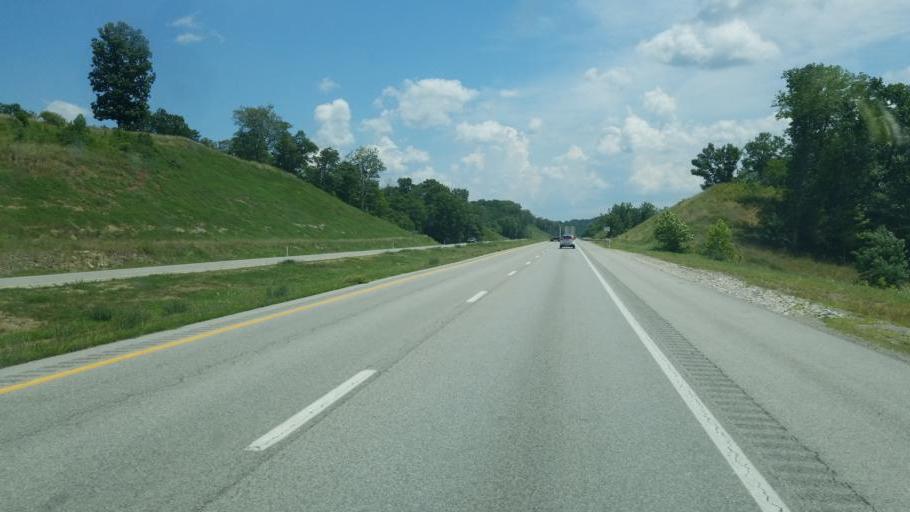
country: US
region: West Virginia
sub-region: Mason County
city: Point Pleasant
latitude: 38.7866
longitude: -82.0849
